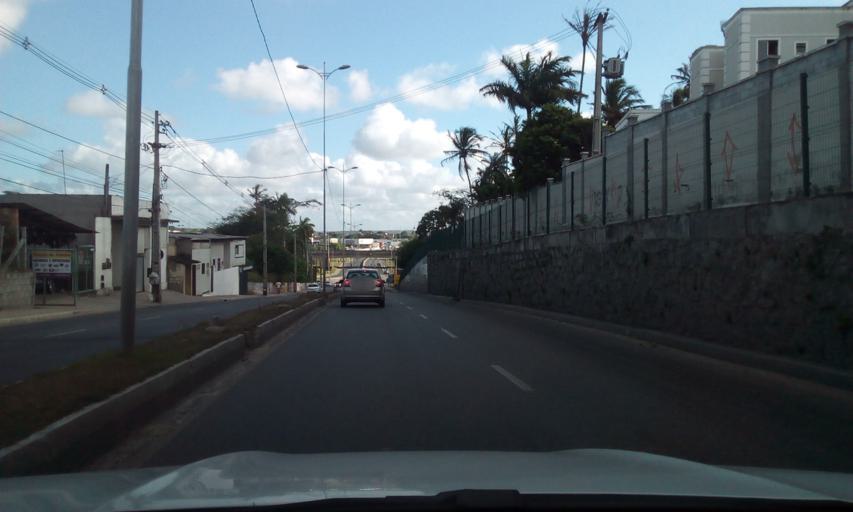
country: BR
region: Paraiba
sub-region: Bayeux
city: Bayeux
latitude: -7.1620
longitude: -34.8964
